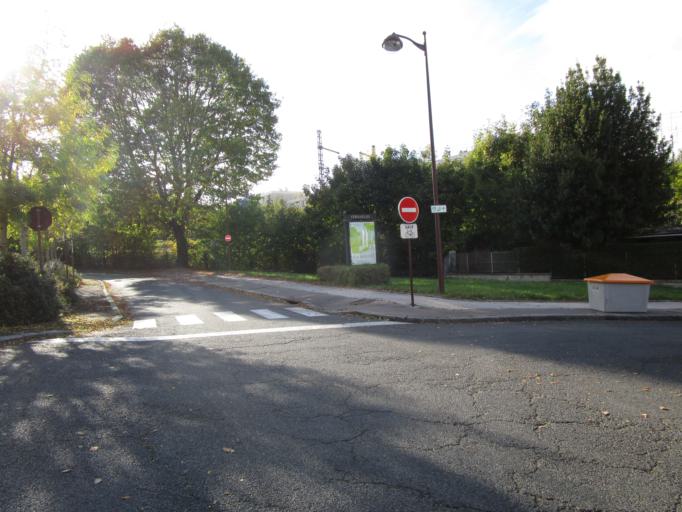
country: FR
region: Ile-de-France
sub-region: Departement des Yvelines
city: Viroflay
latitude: 48.7891
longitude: 2.1525
